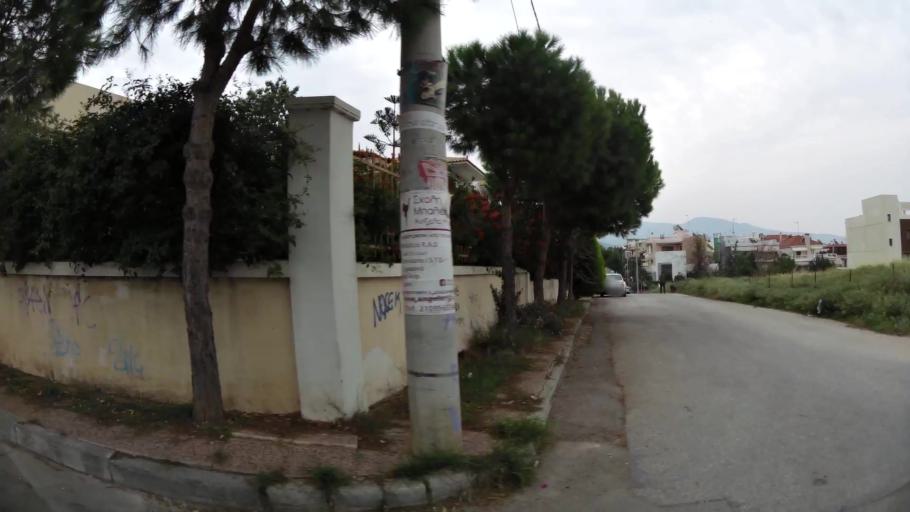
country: GR
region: Attica
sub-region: Nomarchia Athinas
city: Alimos
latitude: 37.9096
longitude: 23.7316
